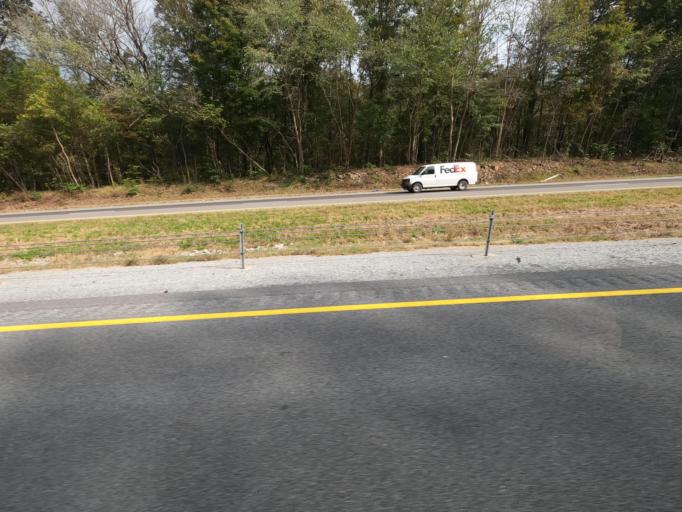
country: US
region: Tennessee
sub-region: Dickson County
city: White Bluff
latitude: 36.0279
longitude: -87.2009
